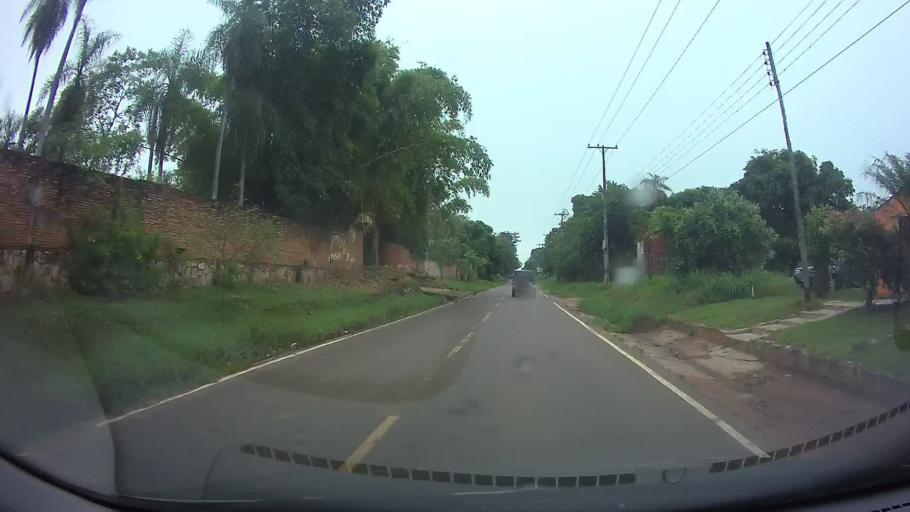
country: PY
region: Central
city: Itaugua
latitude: -25.3680
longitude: -57.3471
